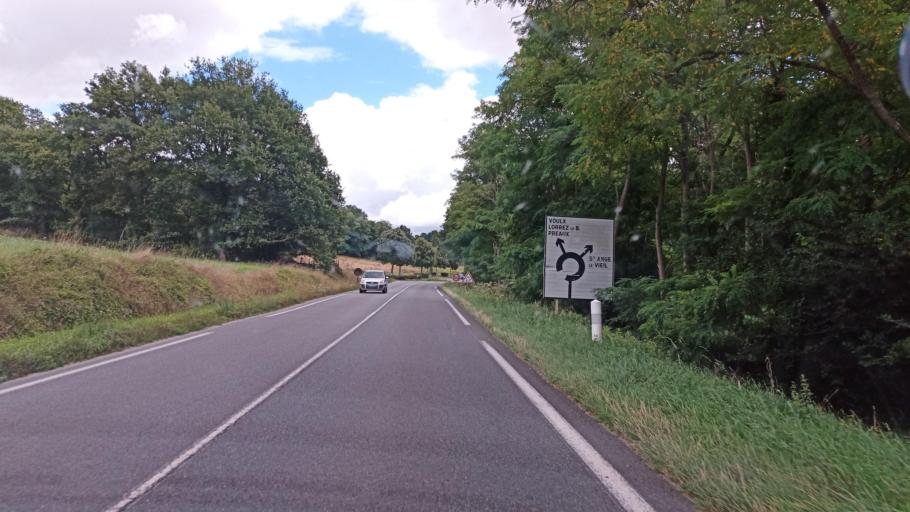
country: FR
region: Ile-de-France
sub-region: Departement de Seine-et-Marne
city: Voulx
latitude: 48.2897
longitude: 2.9537
